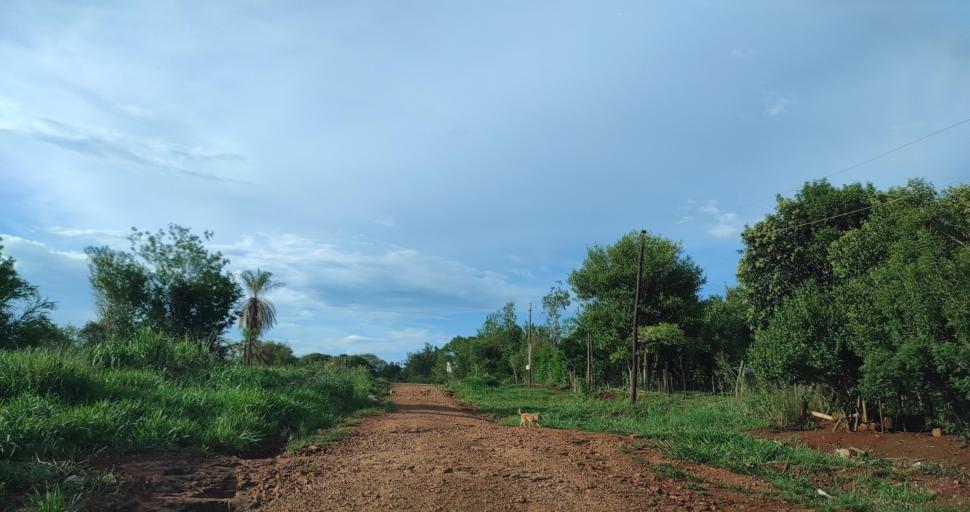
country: AR
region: Misiones
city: Santo Pipo
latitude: -27.1503
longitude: -55.4211
